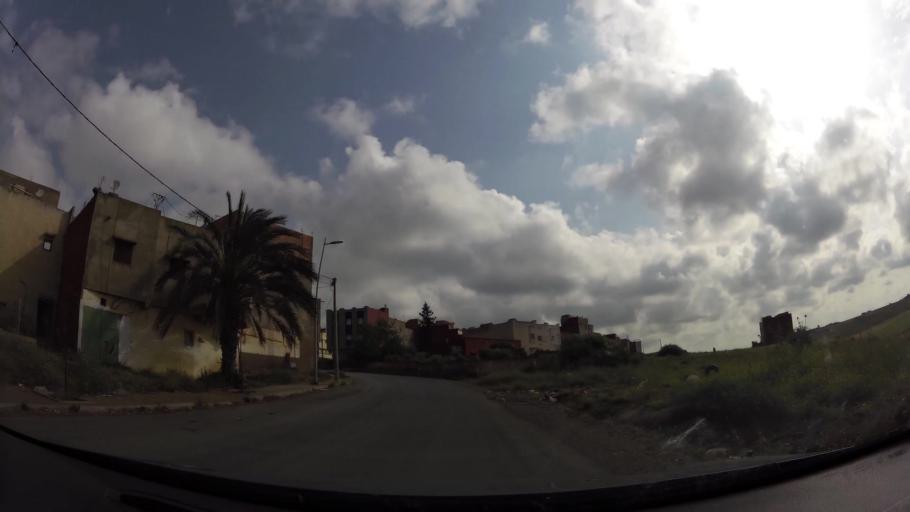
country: MA
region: Rabat-Sale-Zemmour-Zaer
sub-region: Khemisset
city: Tiflet
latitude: 33.8845
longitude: -6.3125
